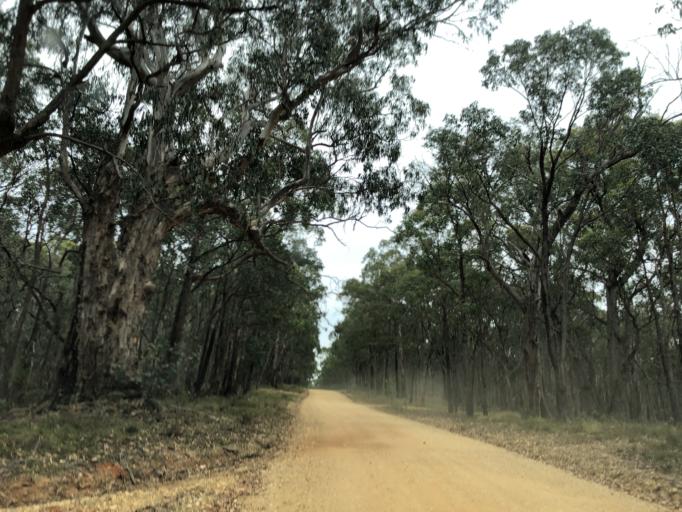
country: AU
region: Victoria
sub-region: Moorabool
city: Bacchus Marsh
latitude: -37.5021
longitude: 144.3262
